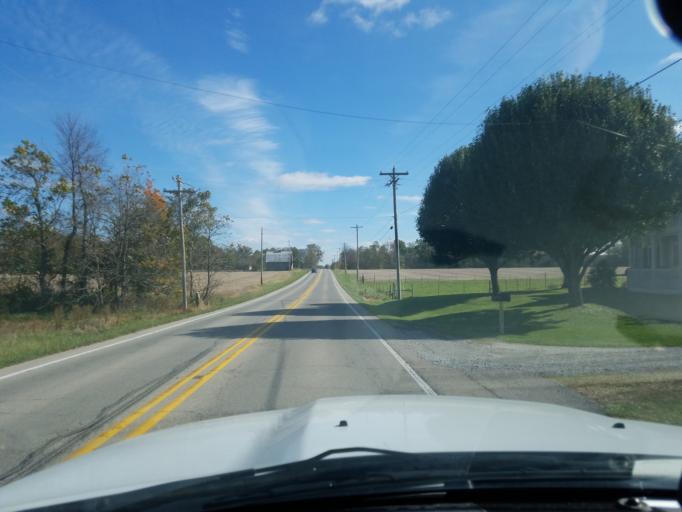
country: US
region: Indiana
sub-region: Ripley County
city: Osgood
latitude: 39.0750
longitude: -85.3637
